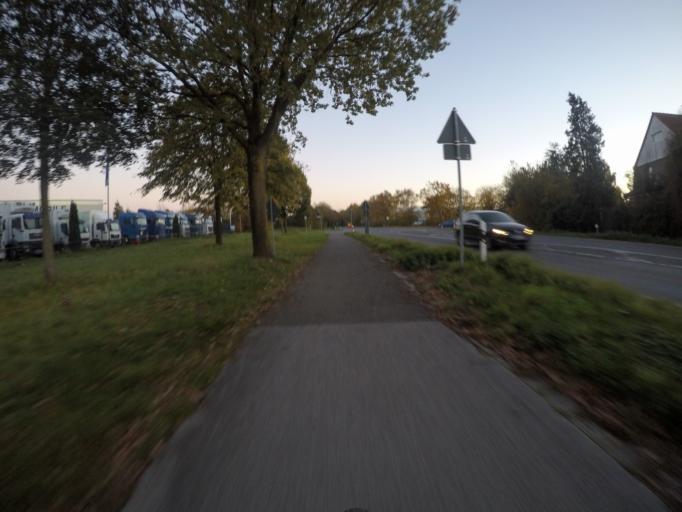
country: DE
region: North Rhine-Westphalia
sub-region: Regierungsbezirk Dusseldorf
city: Bocholt
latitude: 51.8160
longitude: 6.5669
